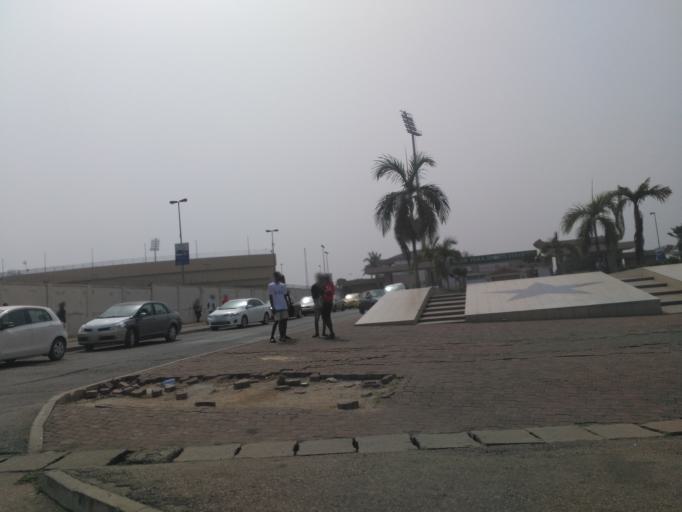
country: GH
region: Ashanti
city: Kumasi
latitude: 6.6847
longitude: -1.6059
